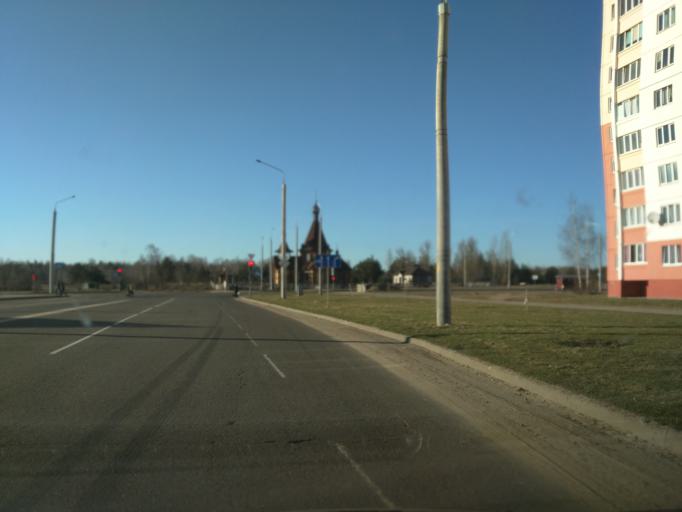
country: BY
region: Mogilev
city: Babruysk
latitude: 53.1668
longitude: 29.1641
